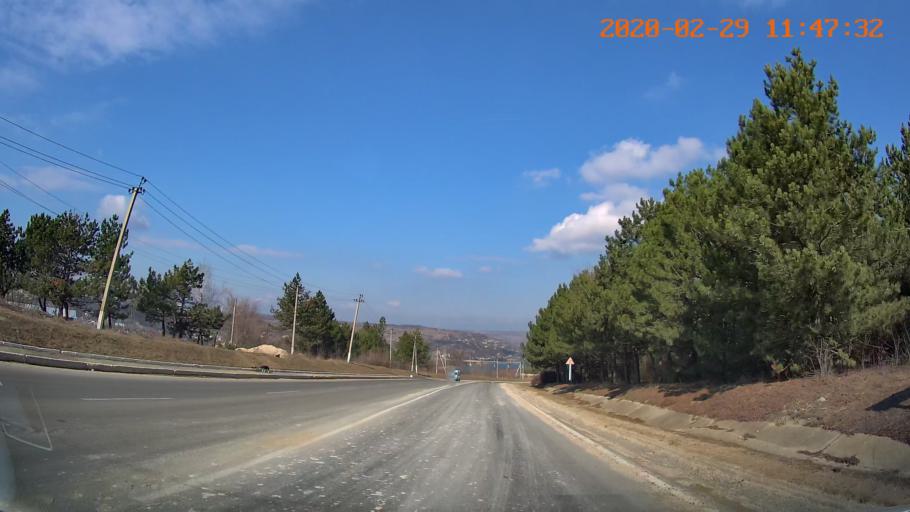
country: MD
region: Rezina
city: Rezina
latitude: 47.7424
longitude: 28.9876
